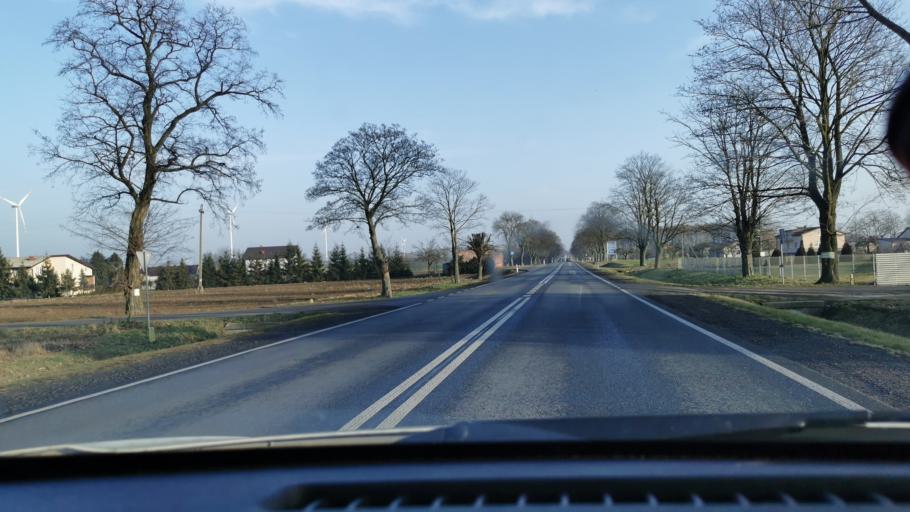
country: PL
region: Lodz Voivodeship
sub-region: Powiat sieradzki
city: Blaszki
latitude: 51.6370
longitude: 18.5208
